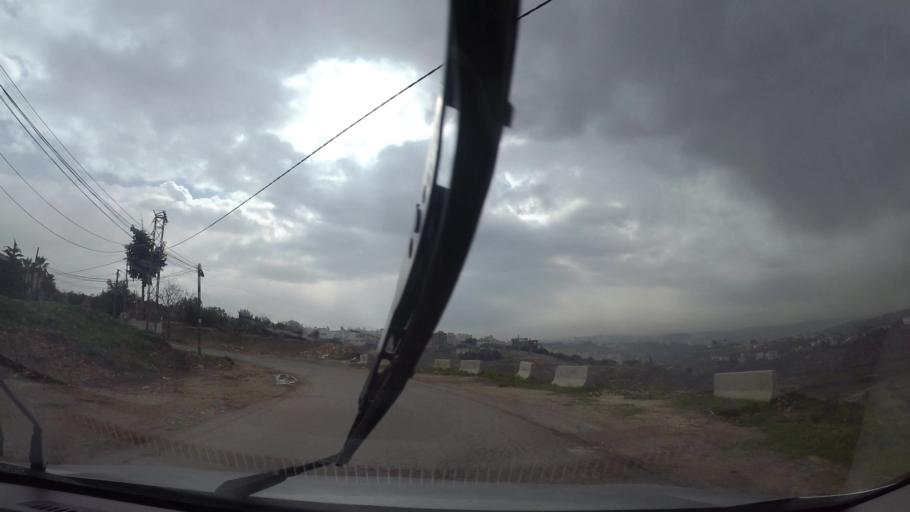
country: JO
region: Amman
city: Wadi as Sir
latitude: 31.9848
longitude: 35.8178
